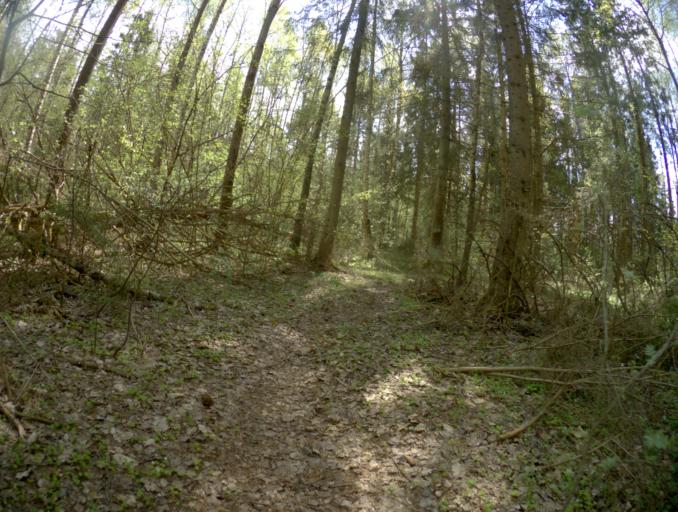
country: RU
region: Vladimir
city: Golovino
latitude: 55.9966
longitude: 40.4141
